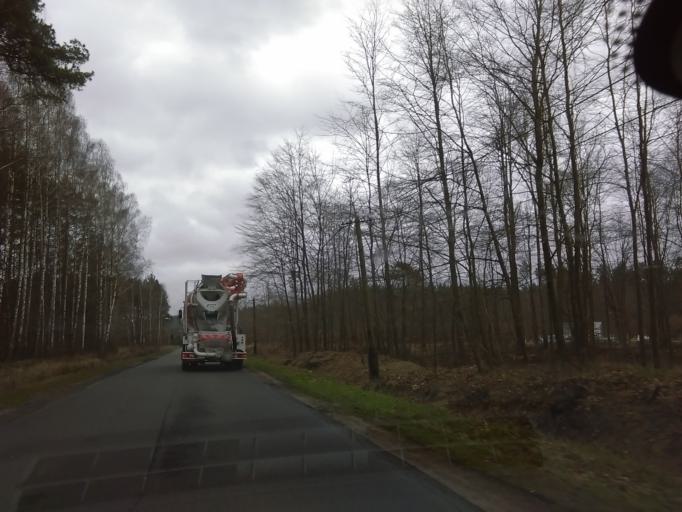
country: PL
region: Greater Poland Voivodeship
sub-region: Powiat zlotowski
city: Lipka
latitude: 53.4863
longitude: 17.2684
